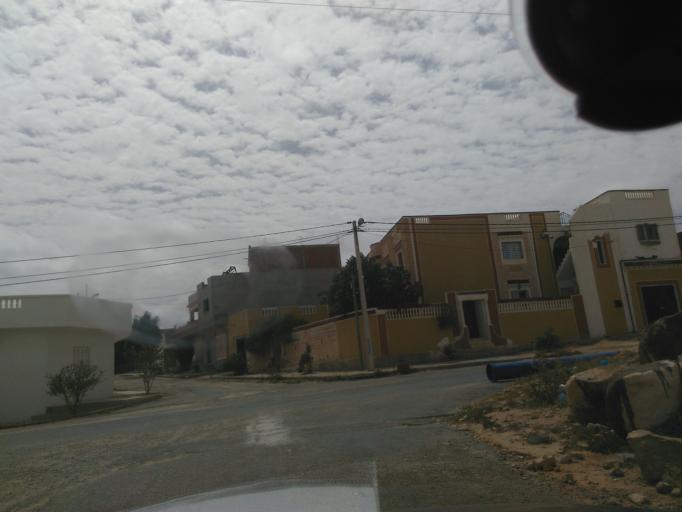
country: TN
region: Tataouine
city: Tataouine
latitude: 32.9470
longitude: 10.4676
